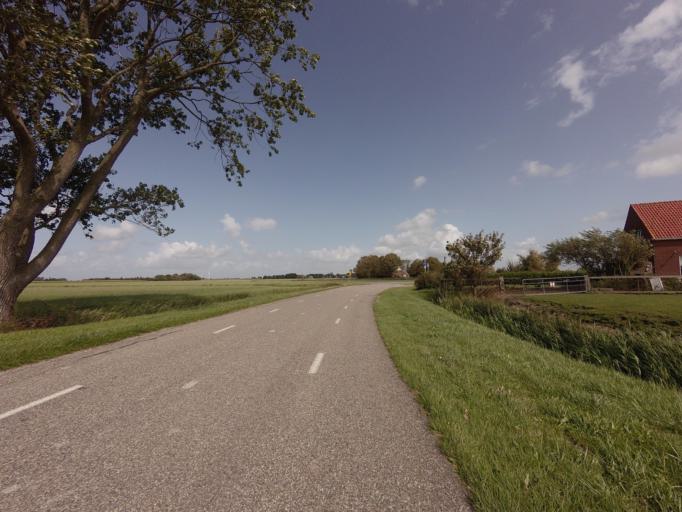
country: NL
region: Friesland
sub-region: Sudwest Fryslan
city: Makkum
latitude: 53.1074
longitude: 5.4325
